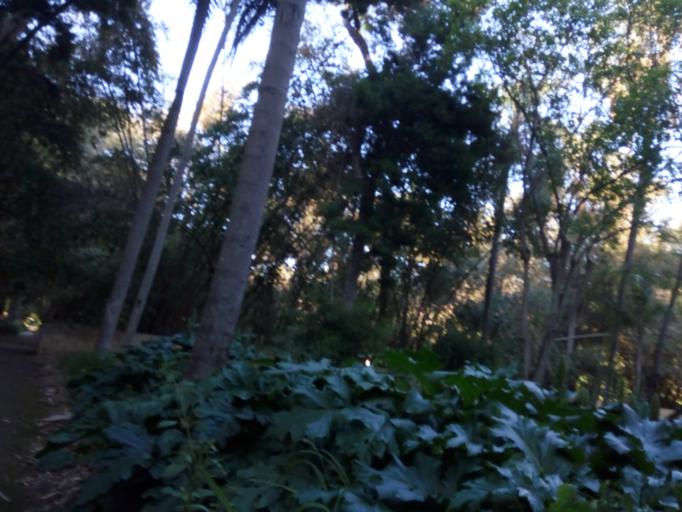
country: DZ
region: Alger
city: Algiers
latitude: 36.7479
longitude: 3.0726
